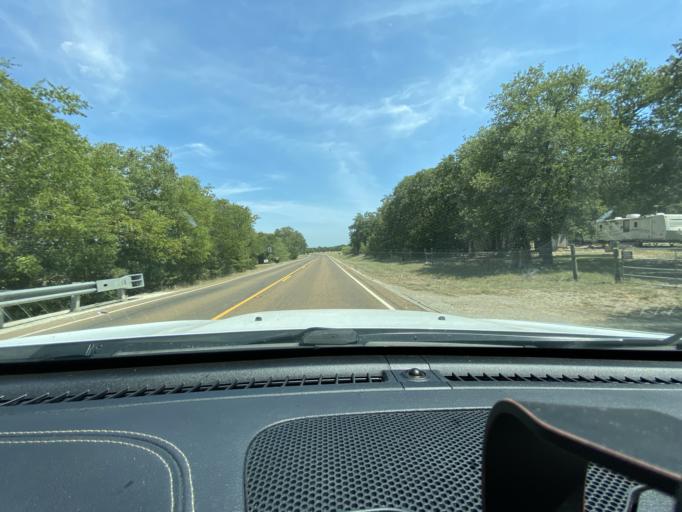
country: US
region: Texas
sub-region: Bastrop County
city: Smithville
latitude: 30.1356
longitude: -97.0798
